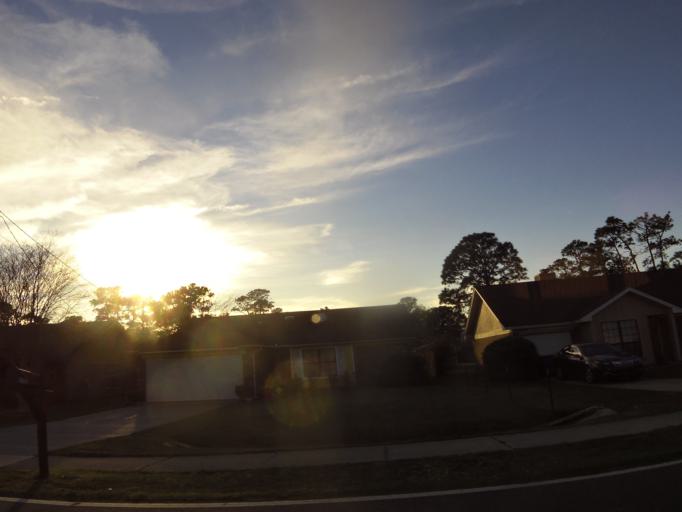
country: US
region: Florida
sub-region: Duval County
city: Jacksonville
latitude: 30.4502
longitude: -81.6700
